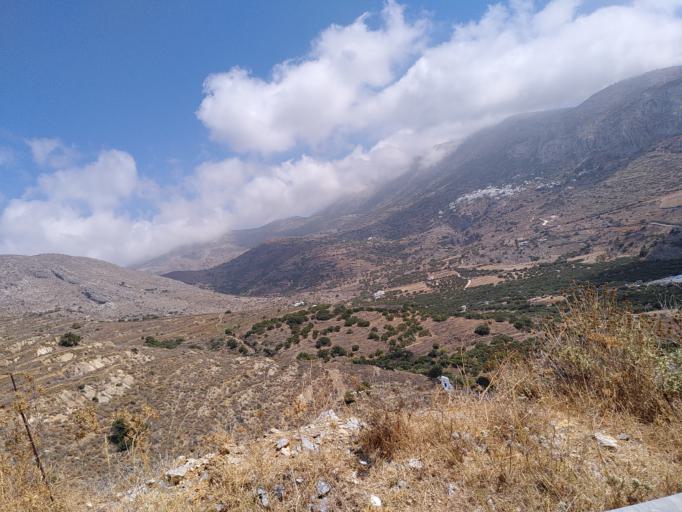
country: GR
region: South Aegean
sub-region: Nomos Kykladon
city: Amorgos
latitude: 36.9106
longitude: 25.9772
